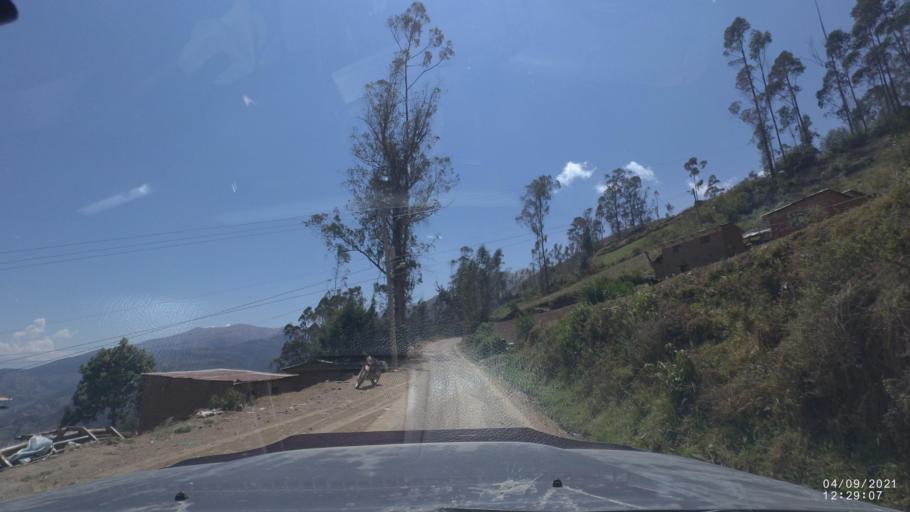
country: BO
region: Cochabamba
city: Colchani
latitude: -17.2260
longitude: -66.5252
